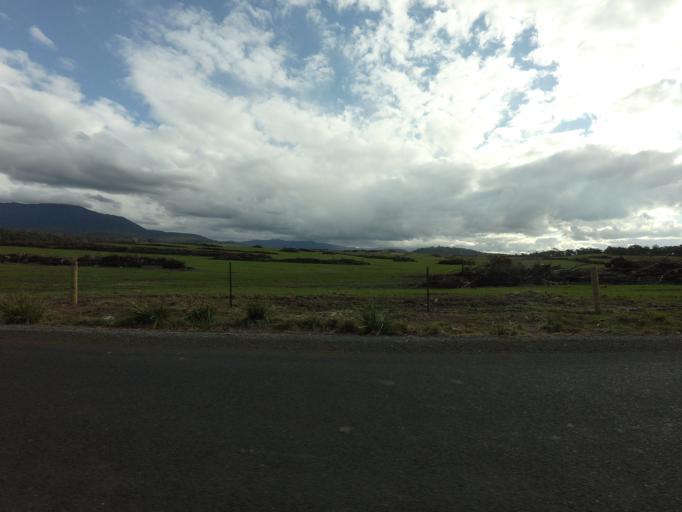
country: AU
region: Tasmania
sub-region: Northern Midlands
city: Longford
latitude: -41.8474
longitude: 147.2142
